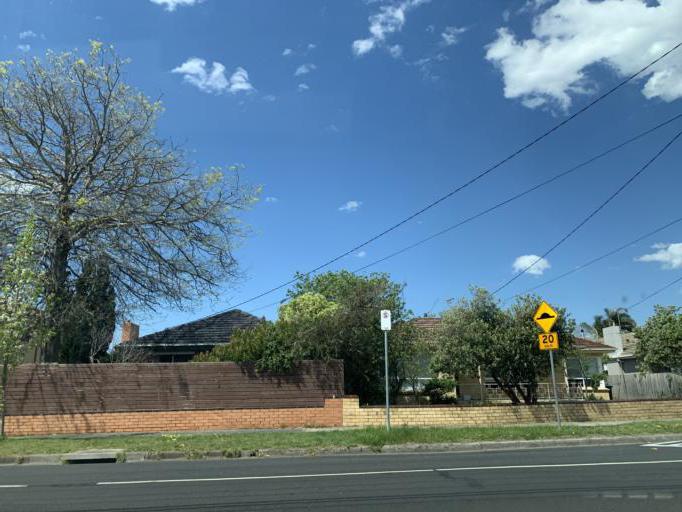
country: AU
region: Victoria
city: Highett
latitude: -37.9415
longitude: 145.0478
